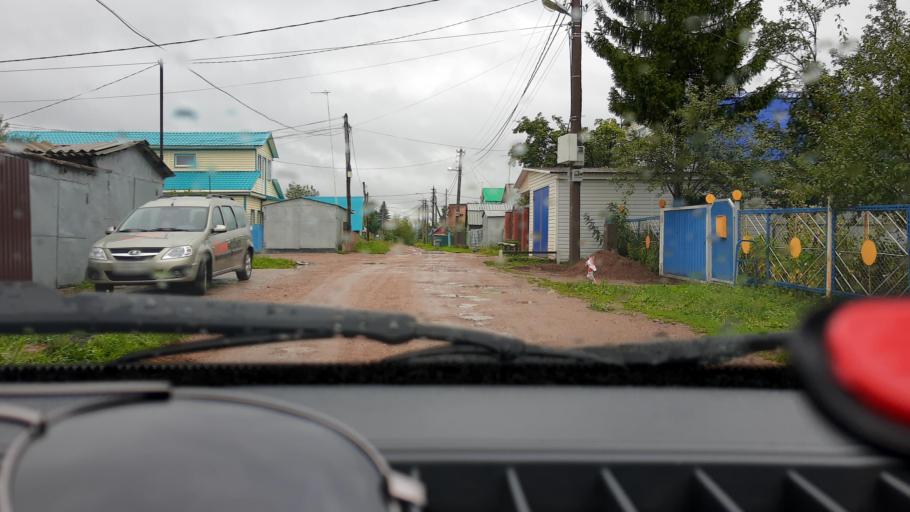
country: RU
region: Bashkortostan
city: Ufa
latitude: 54.8381
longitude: 56.1537
